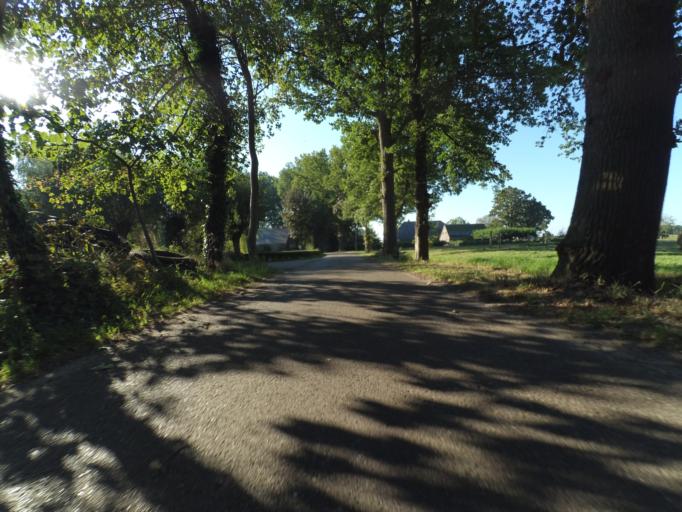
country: NL
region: Gelderland
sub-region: Gemeente Barneveld
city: Voorthuizen
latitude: 52.1813
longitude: 5.5603
